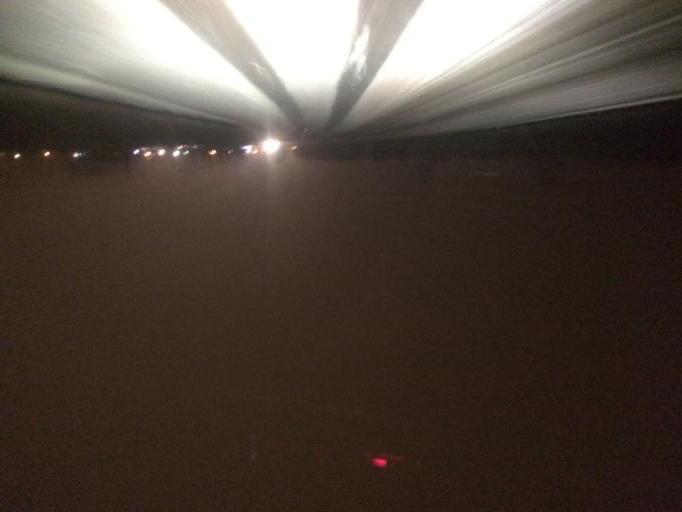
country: RU
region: Tula
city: Kosaya Gora
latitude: 54.1610
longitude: 37.4578
